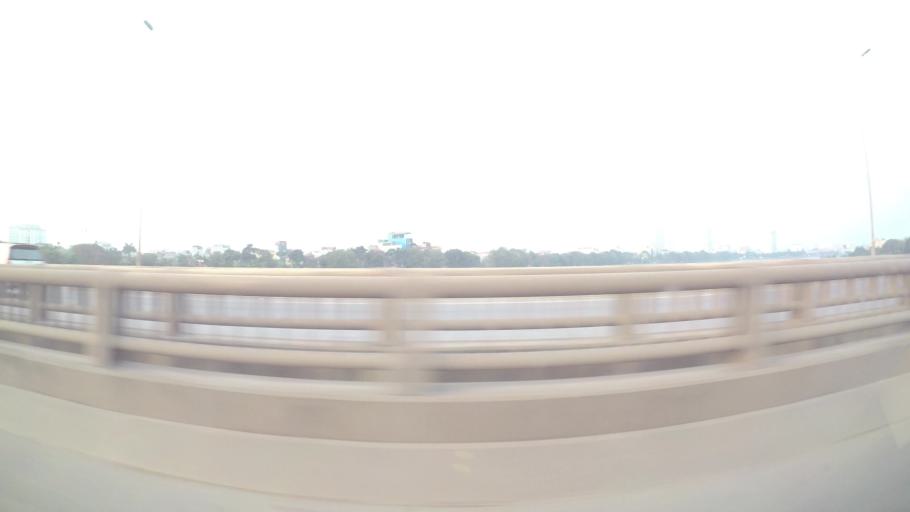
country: VN
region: Ha Noi
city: Van Dien
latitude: 20.9678
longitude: 105.8312
